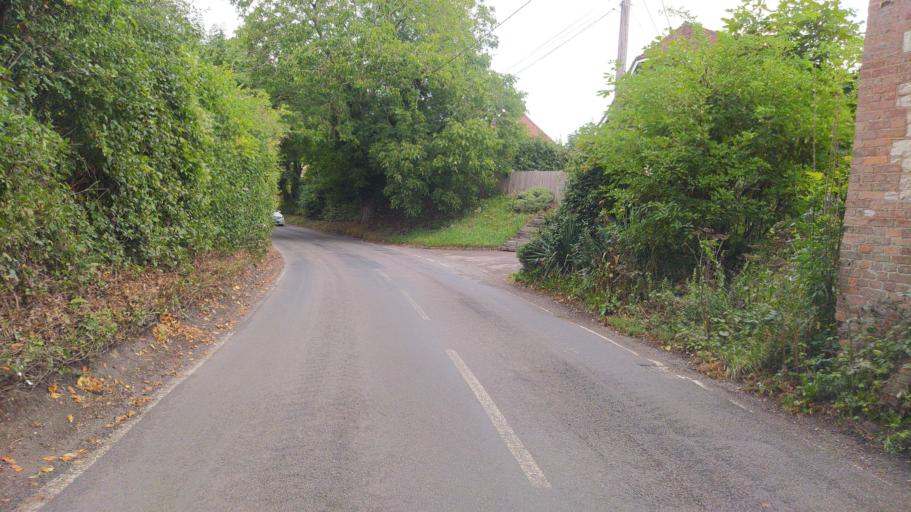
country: GB
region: England
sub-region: Hampshire
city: Petersfield
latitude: 50.9661
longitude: -0.8841
